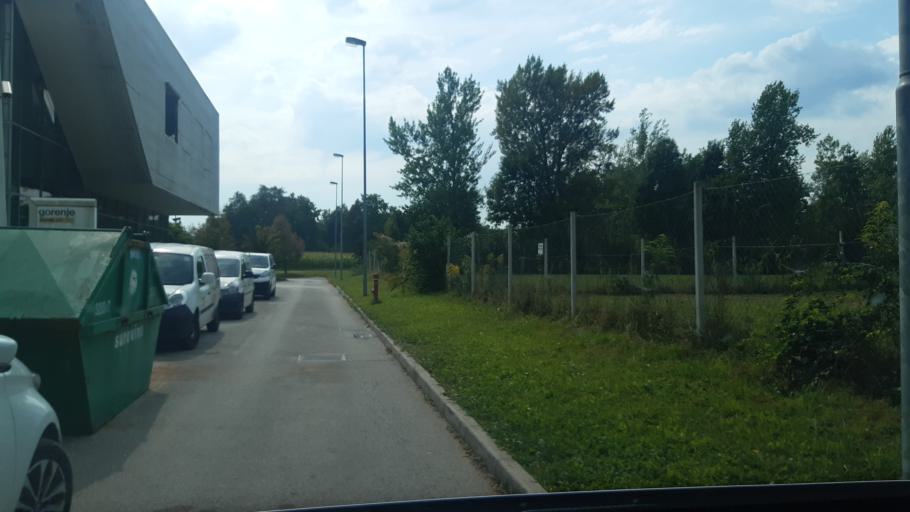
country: SI
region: Trzin
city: Trzin
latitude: 46.0954
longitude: 14.5510
